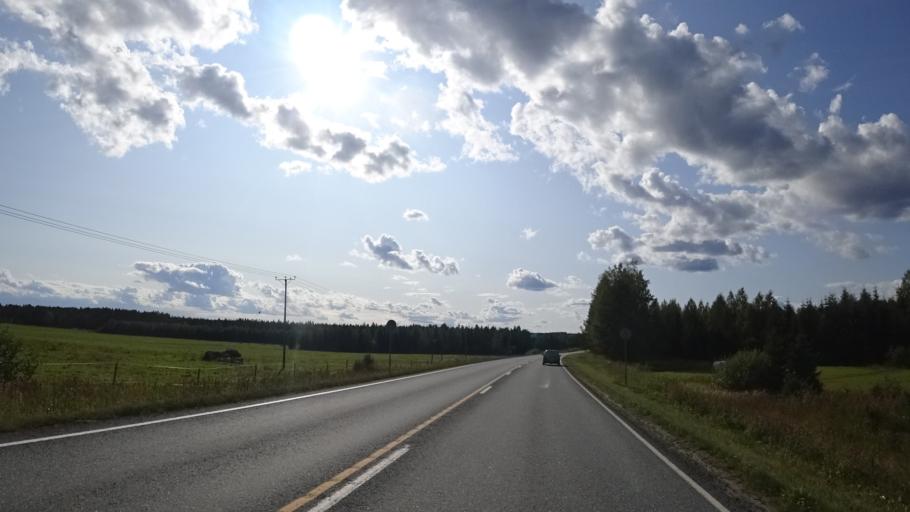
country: FI
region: North Karelia
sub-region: Keski-Karjala
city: Kitee
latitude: 62.0884
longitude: 30.0000
